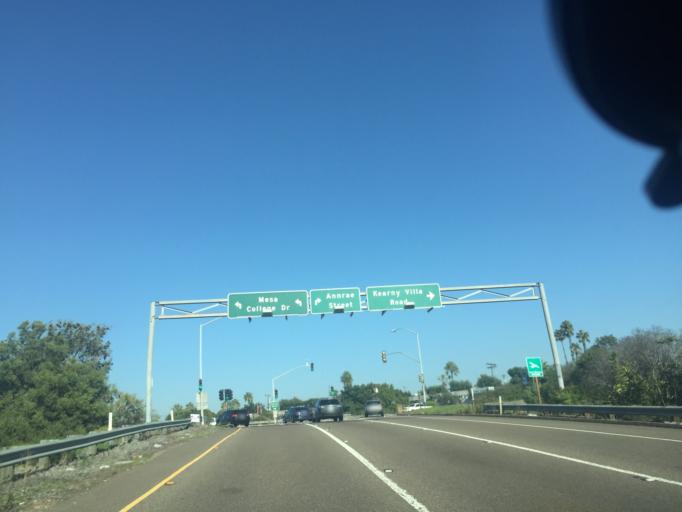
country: US
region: California
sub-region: San Diego County
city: San Diego
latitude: 32.8015
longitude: -117.1549
